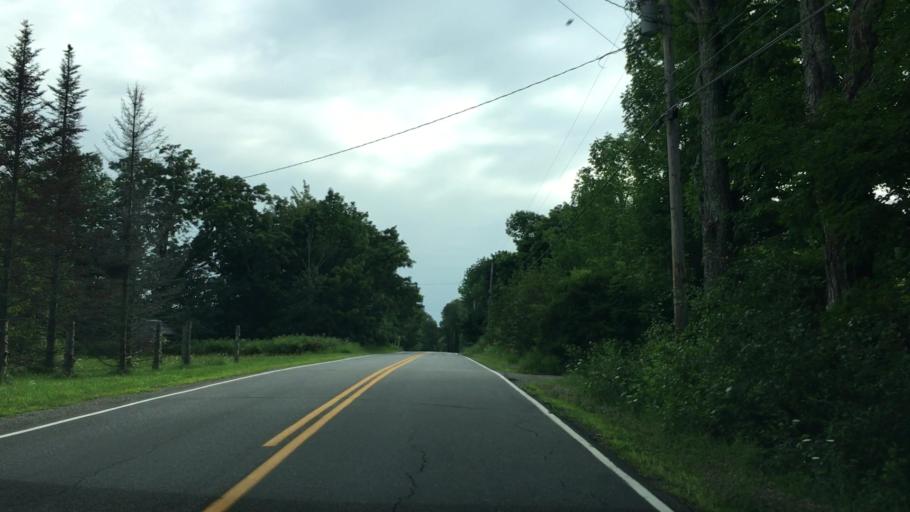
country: US
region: Maine
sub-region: Waldo County
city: Belfast
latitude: 44.3675
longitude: -69.0392
